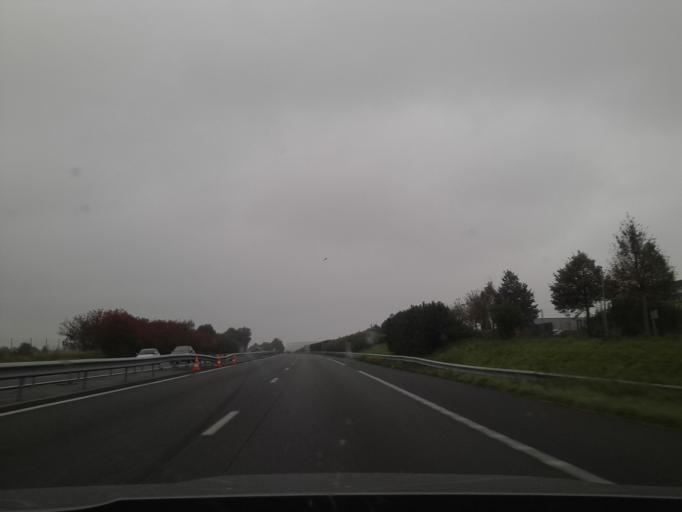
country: FR
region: Nord-Pas-de-Calais
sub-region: Departement du Nord
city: Neuville-Saint-Remy
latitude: 50.1914
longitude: 3.1988
